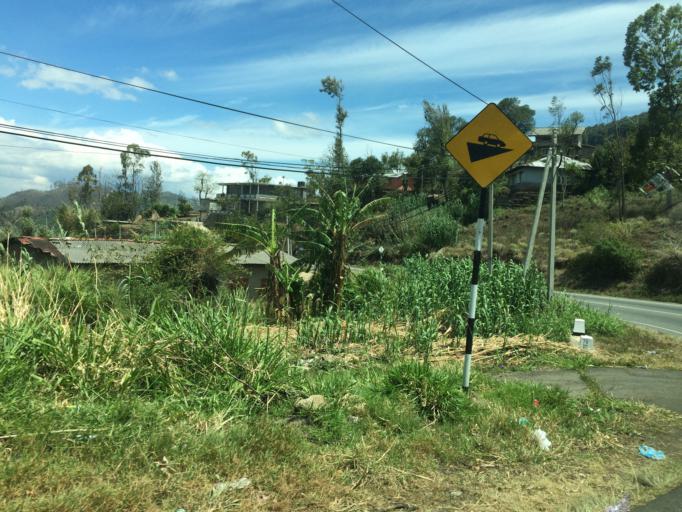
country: LK
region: Central
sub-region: Nuwara Eliya District
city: Nuwara Eliya
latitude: 6.9102
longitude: 80.8364
